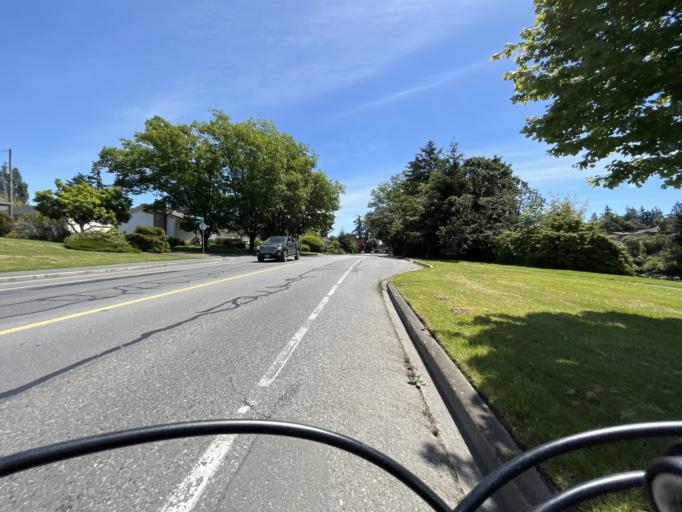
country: CA
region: British Columbia
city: Victoria
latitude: 48.4511
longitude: -123.4148
